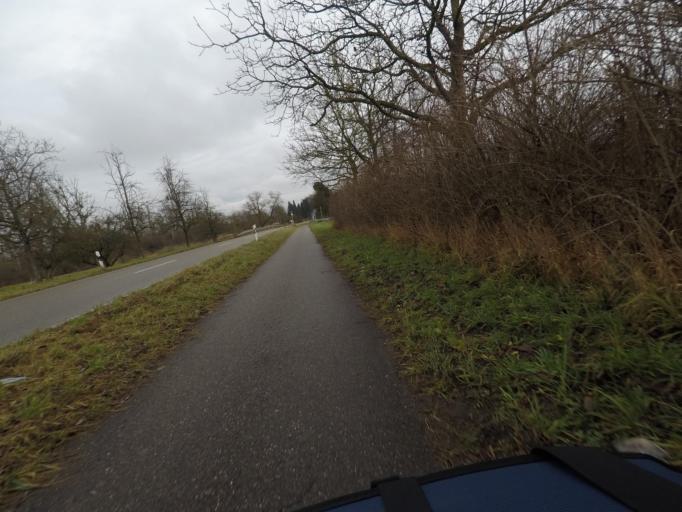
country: DE
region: Baden-Wuerttemberg
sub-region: Karlsruhe Region
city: Au am Rhein
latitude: 48.9603
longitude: 8.2473
